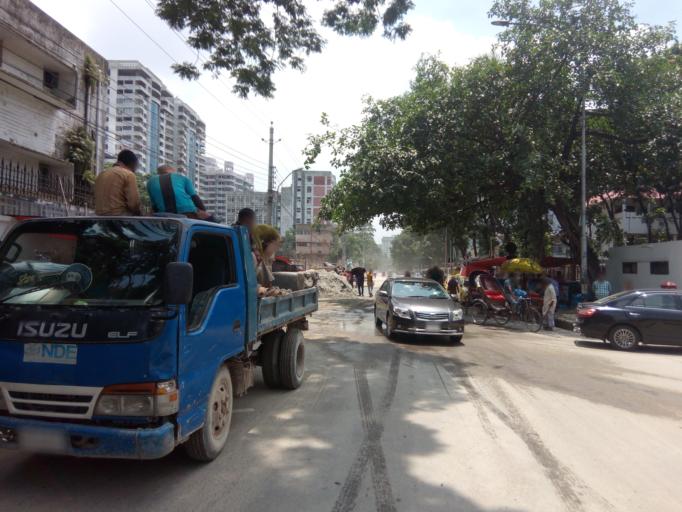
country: BD
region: Dhaka
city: Paltan
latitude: 23.7461
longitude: 90.4030
